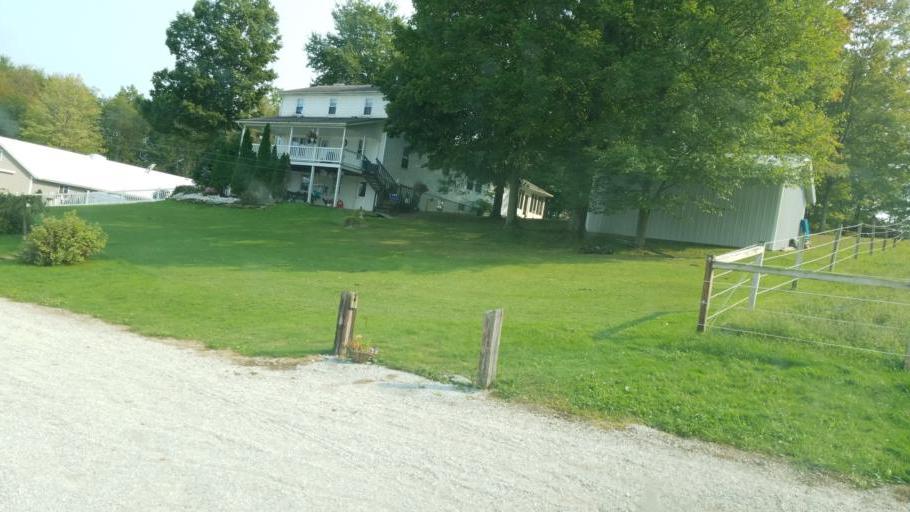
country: US
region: Ohio
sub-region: Ashtabula County
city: Orwell
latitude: 41.4790
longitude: -80.9529
